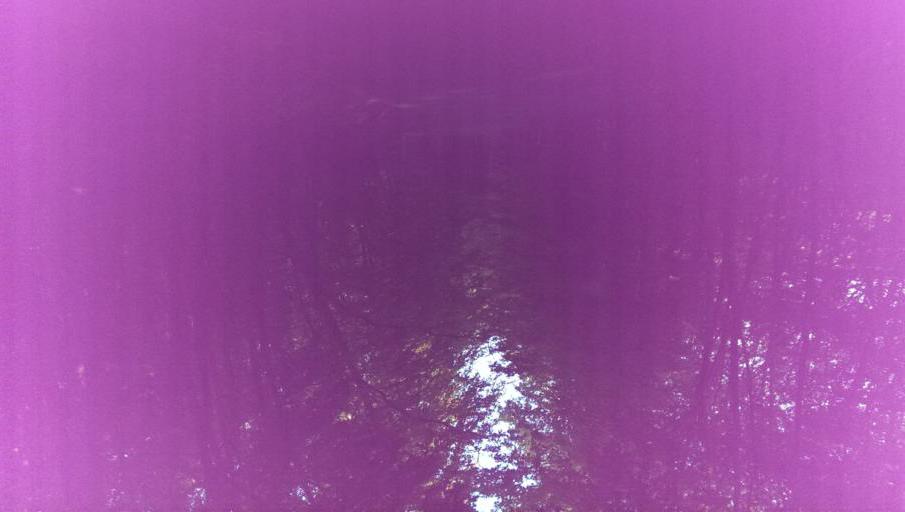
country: CZ
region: Zlin
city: Korycany
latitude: 49.0924
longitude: 17.1814
